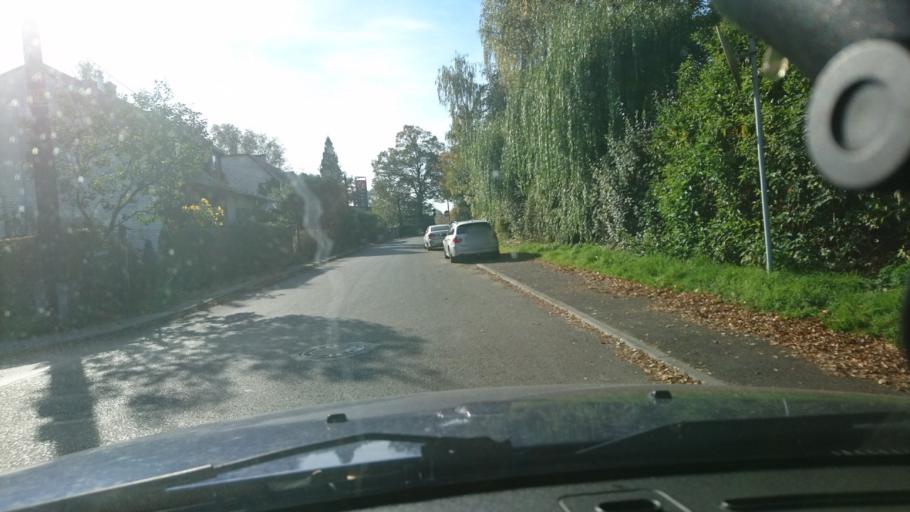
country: PL
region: Silesian Voivodeship
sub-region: Bielsko-Biala
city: Bielsko-Biala
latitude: 49.8367
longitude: 19.0409
